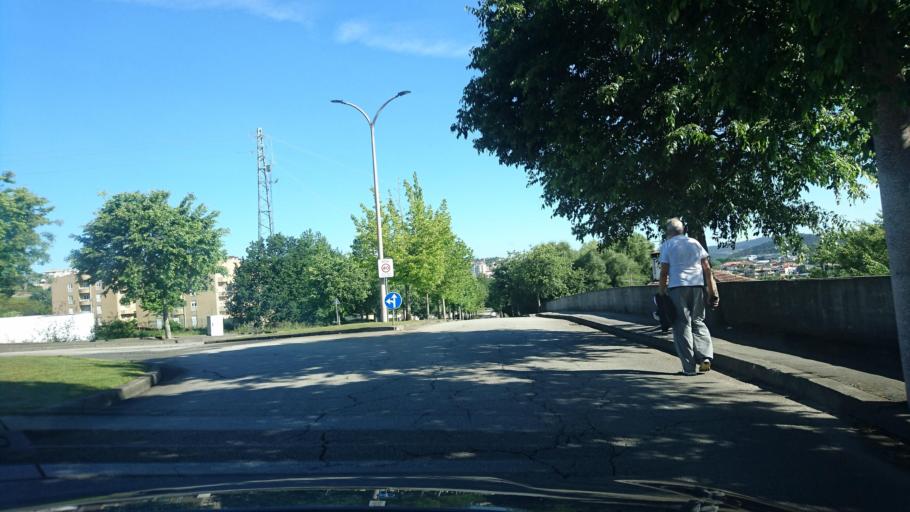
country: PT
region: Aveiro
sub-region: Sao Joao da Madeira
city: Sao Joao da Madeira
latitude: 40.8897
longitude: -8.4842
